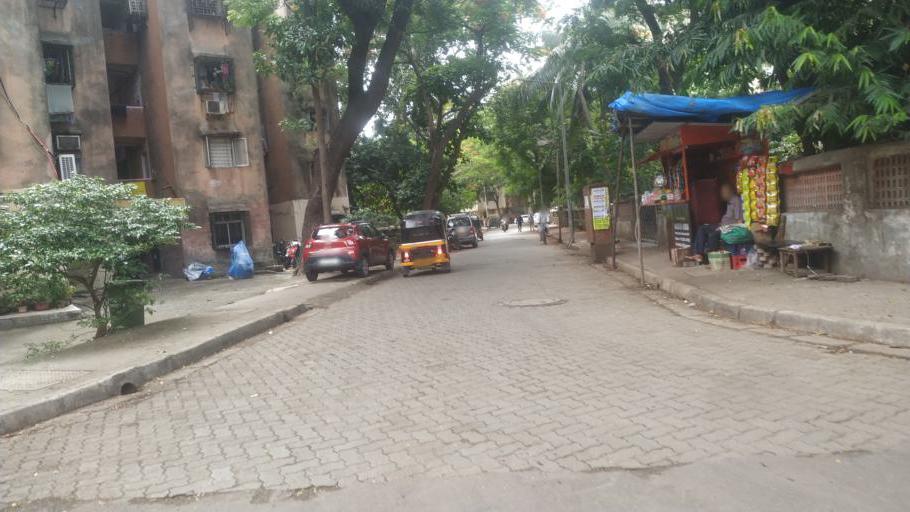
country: IN
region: Maharashtra
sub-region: Mumbai Suburban
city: Mumbai
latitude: 19.0670
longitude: 72.8916
